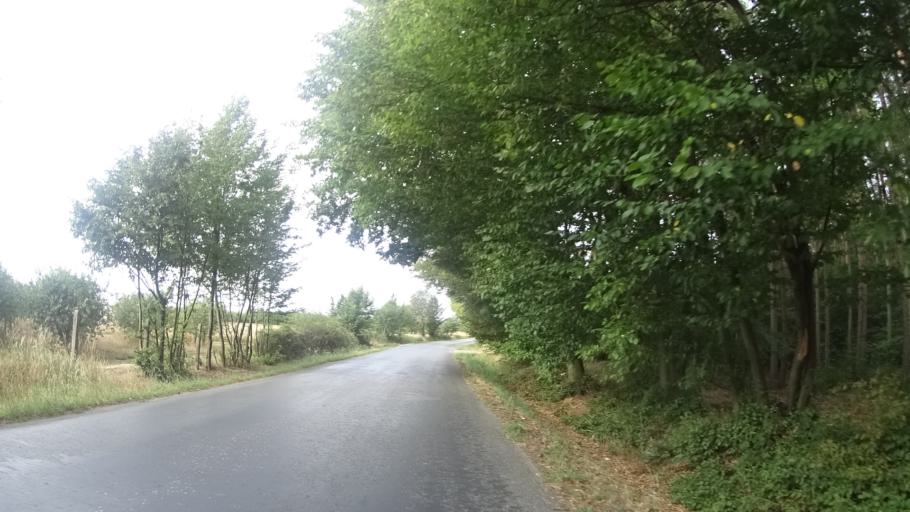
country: CZ
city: Stezery
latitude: 50.2092
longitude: 15.7210
